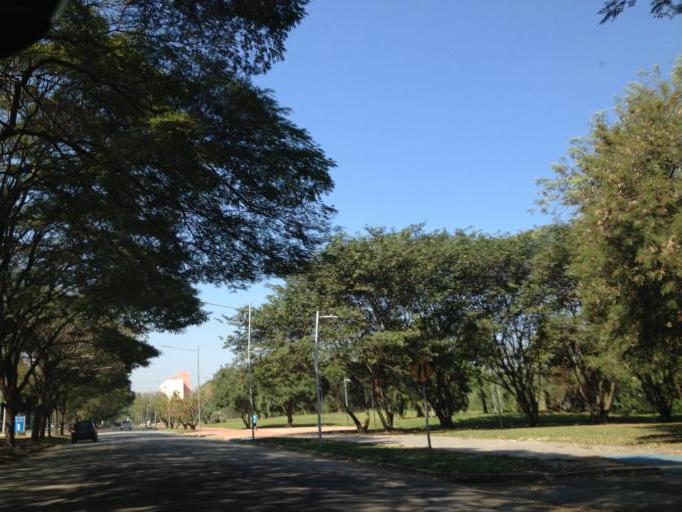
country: BR
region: Sao Paulo
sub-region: Osasco
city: Osasco
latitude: -23.5555
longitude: -46.7236
